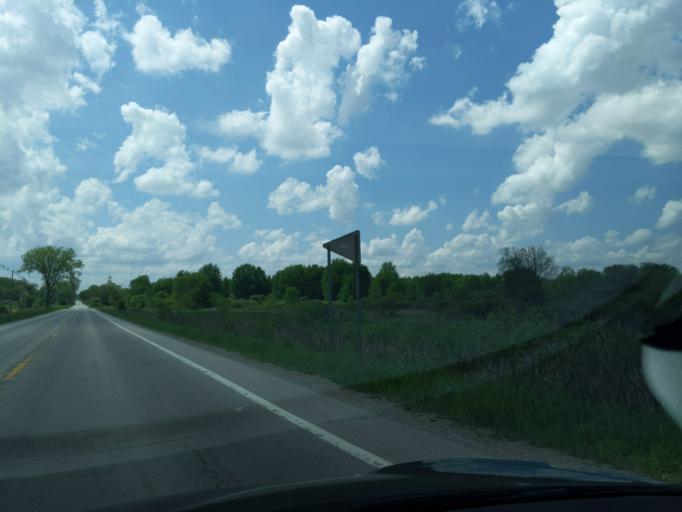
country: US
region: Michigan
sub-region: Ingham County
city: Mason
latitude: 42.5559
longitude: -84.3368
